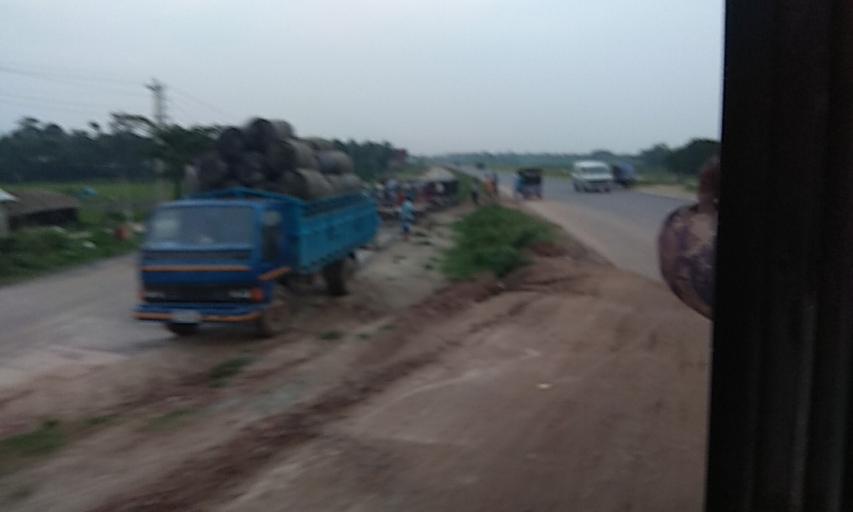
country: BD
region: Dhaka
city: Char Bhadrasan
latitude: 23.3805
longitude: 90.0058
